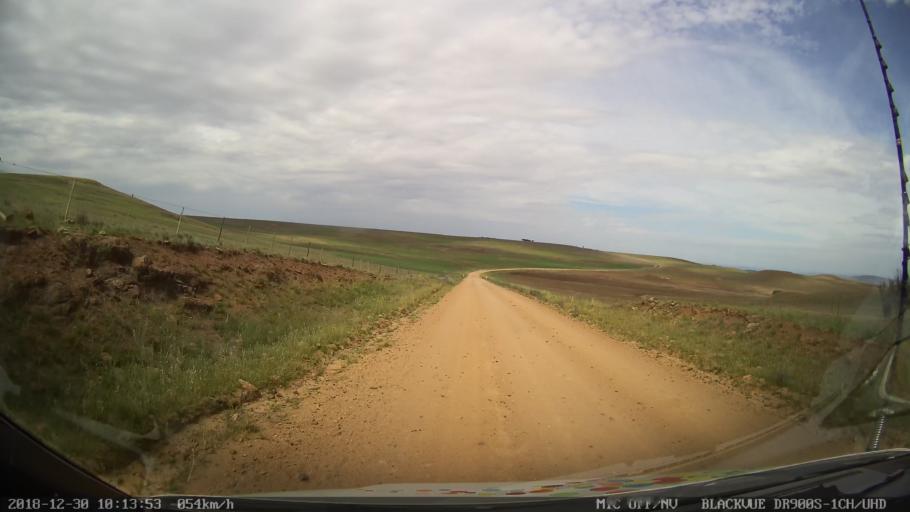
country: AU
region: New South Wales
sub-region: Snowy River
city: Berridale
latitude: -36.5397
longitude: 149.0612
